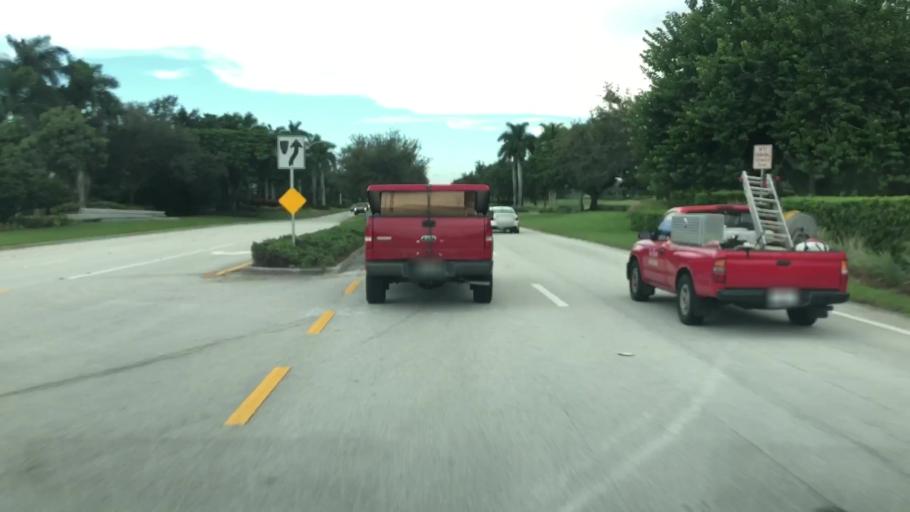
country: US
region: Florida
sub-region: Broward County
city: Parkland
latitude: 26.3137
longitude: -80.2790
